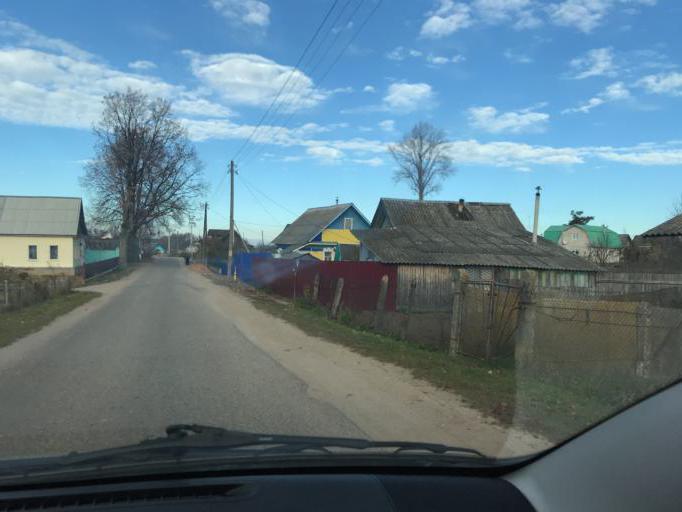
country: BY
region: Vitebsk
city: Haradok
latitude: 55.4599
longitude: 30.0063
